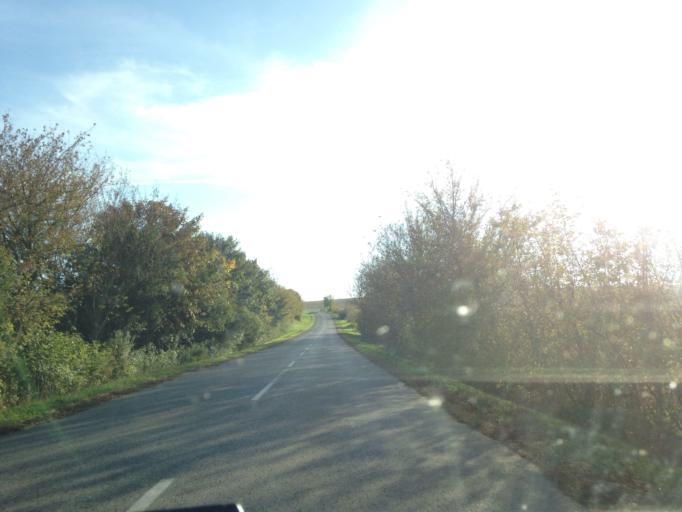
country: SK
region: Nitriansky
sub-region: Okres Komarno
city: Hurbanovo
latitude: 47.8804
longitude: 18.2883
